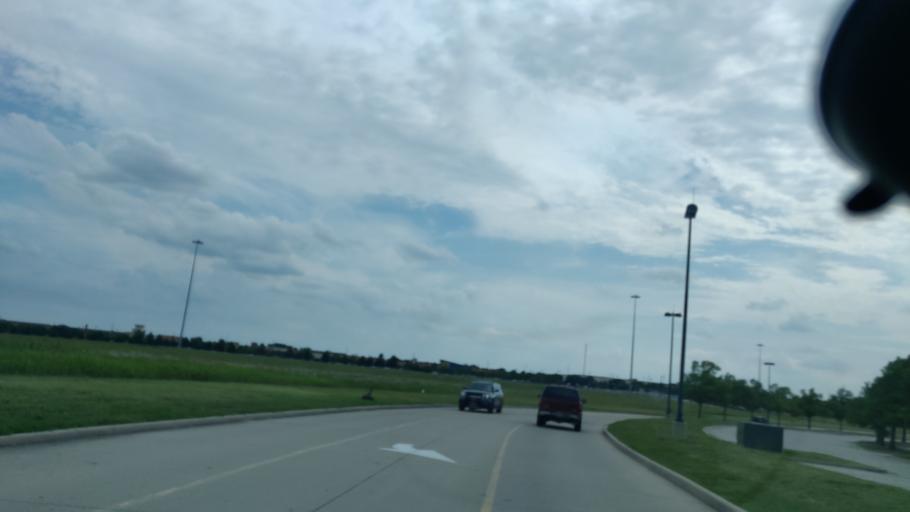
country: US
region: Texas
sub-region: Dallas County
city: Sachse
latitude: 32.9503
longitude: -96.6112
